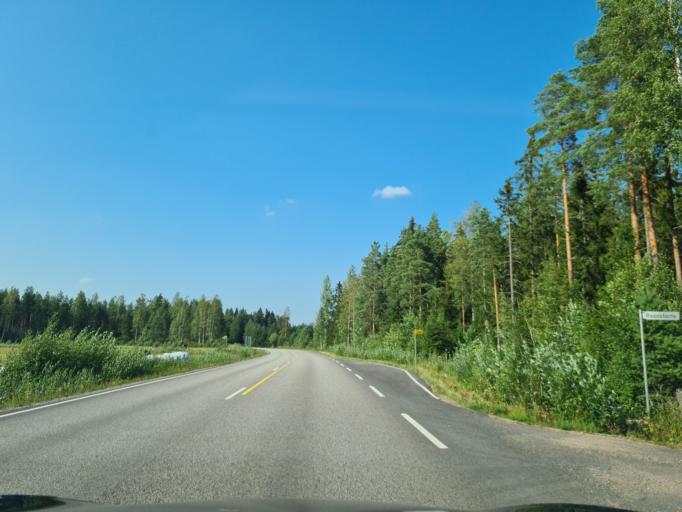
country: FI
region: Satakunta
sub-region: Pohjois-Satakunta
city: Karvia
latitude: 62.1898
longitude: 22.5971
